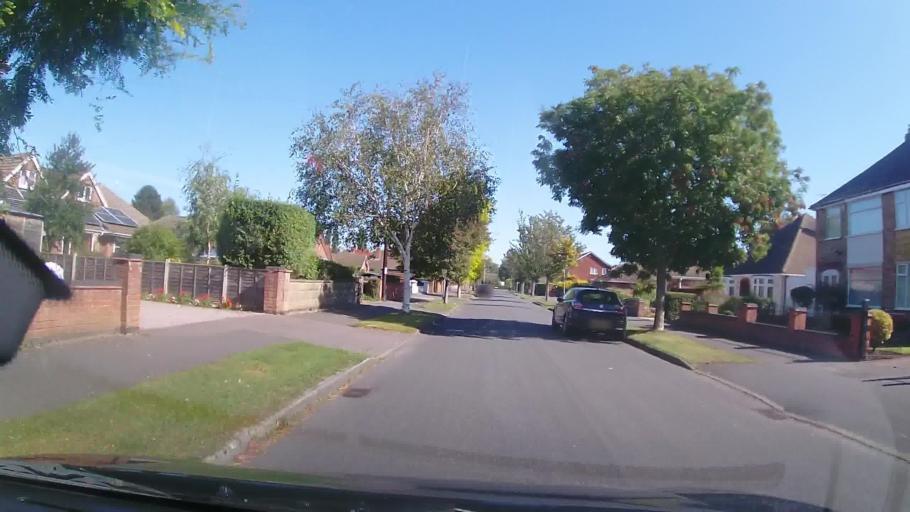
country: GB
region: England
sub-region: Leicestershire
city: Glenfield
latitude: 52.6421
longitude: -1.1945
